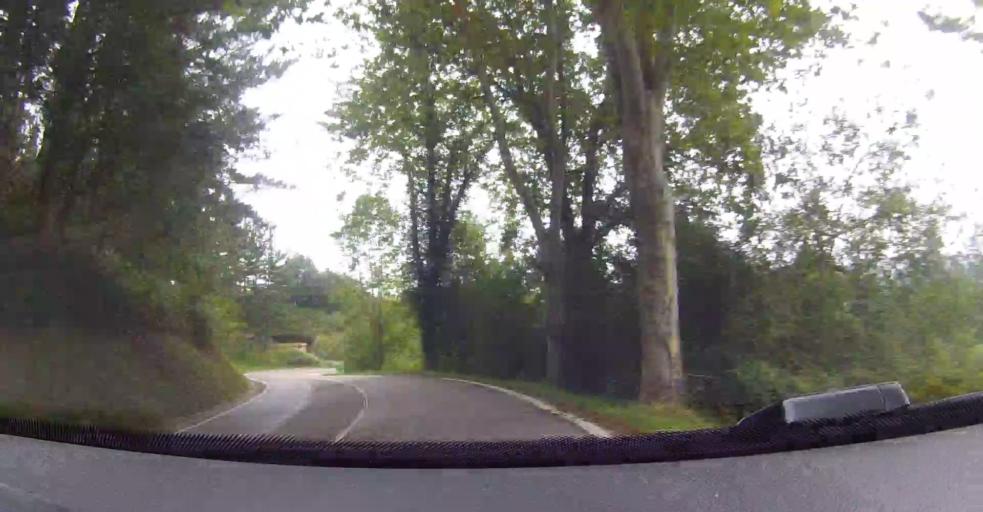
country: ES
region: Basque Country
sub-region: Bizkaia
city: Balmaseda
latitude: 43.2499
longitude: -3.2768
